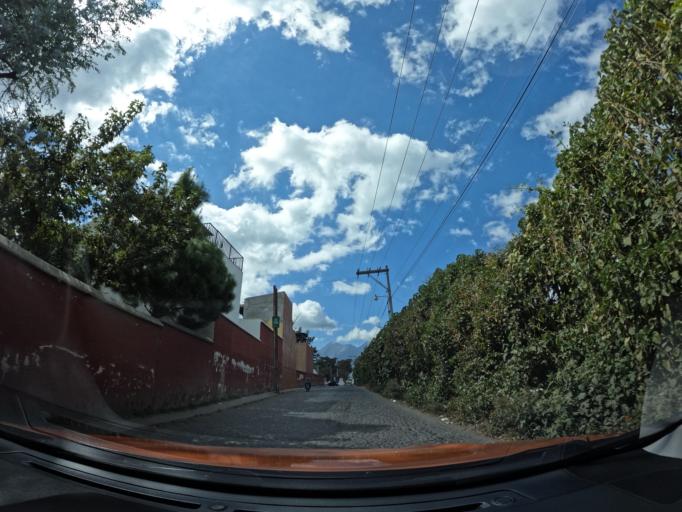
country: GT
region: Sacatepequez
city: Ciudad Vieja
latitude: 14.5286
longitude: -90.7435
